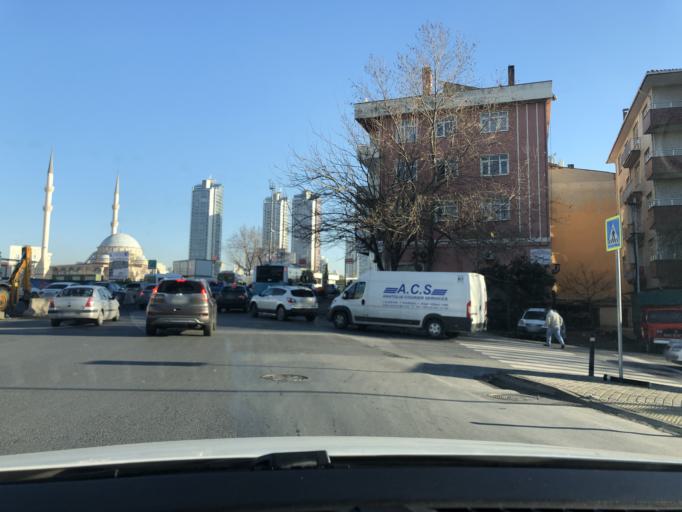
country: TR
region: Istanbul
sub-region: Atasehir
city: Atasehir
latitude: 40.9783
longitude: 29.1259
